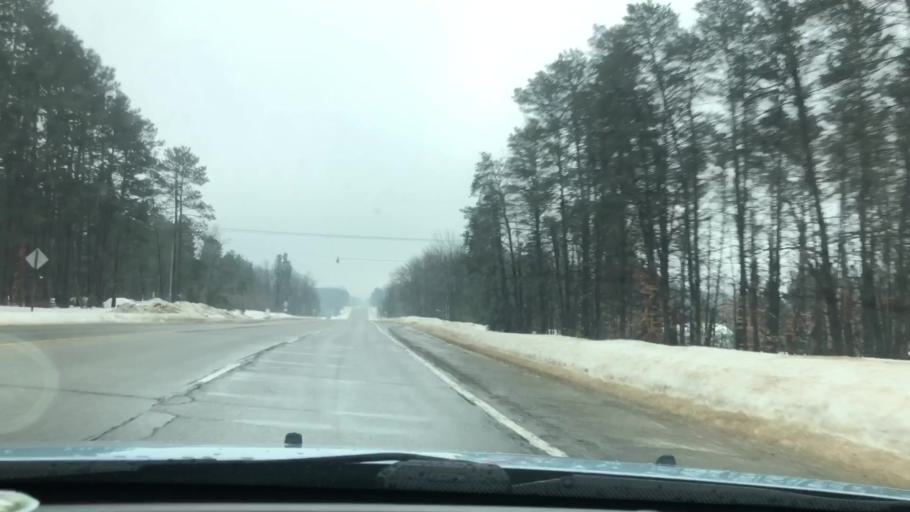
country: US
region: Michigan
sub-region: Otsego County
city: Gaylord
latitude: 45.0584
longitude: -84.7760
